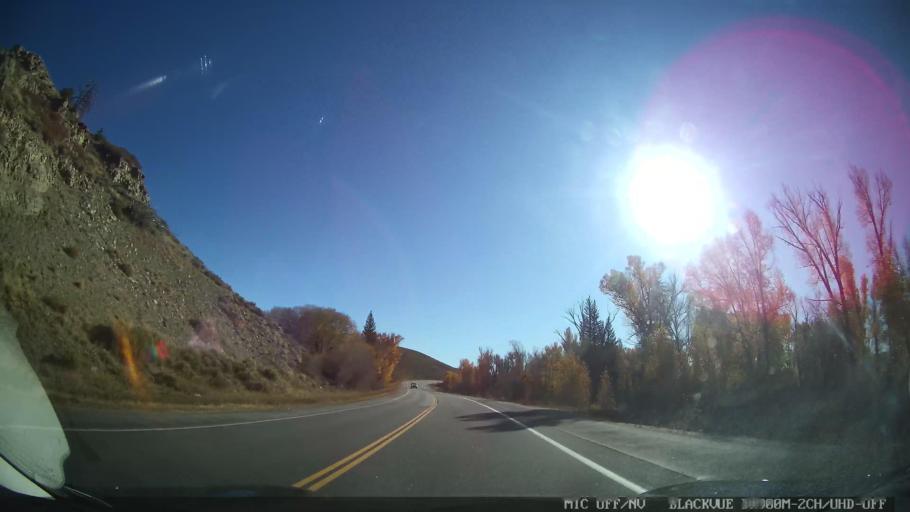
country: US
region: Colorado
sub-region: Grand County
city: Granby
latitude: 40.1108
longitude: -105.9937
